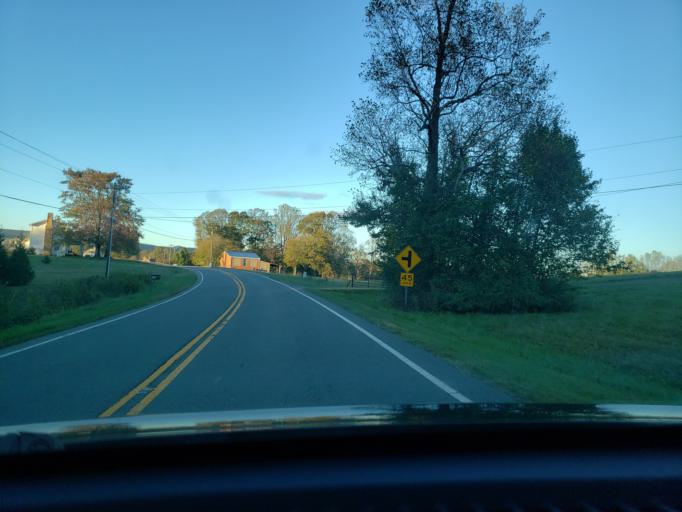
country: US
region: North Carolina
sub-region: Stokes County
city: Danbury
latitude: 36.3284
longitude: -80.2250
